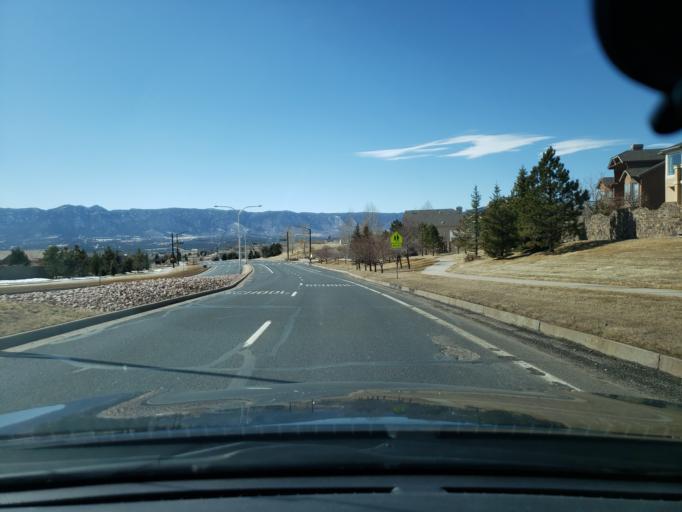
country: US
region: Colorado
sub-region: El Paso County
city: Gleneagle
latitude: 39.0301
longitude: -104.7881
